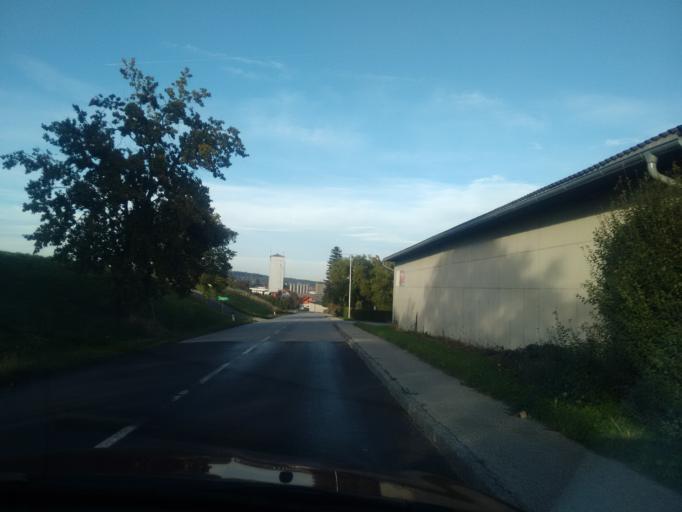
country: AT
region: Upper Austria
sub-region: Politischer Bezirk Vocklabruck
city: Niederthalheim
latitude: 48.1325
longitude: 13.7259
